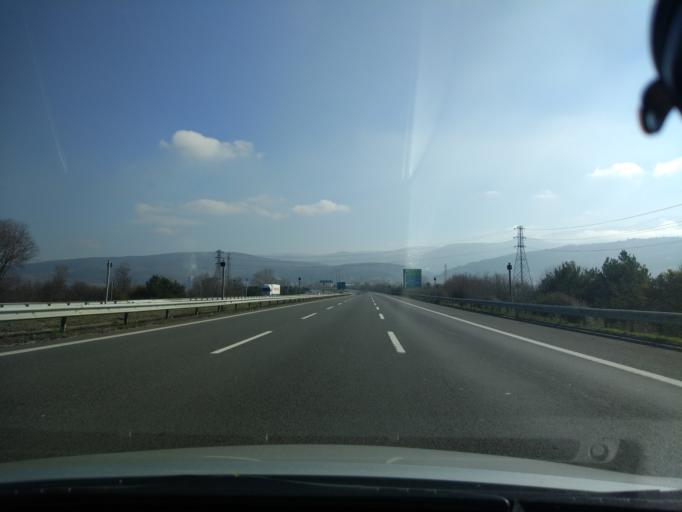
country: TR
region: Bolu
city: Bolu
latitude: 40.7647
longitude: 31.7544
